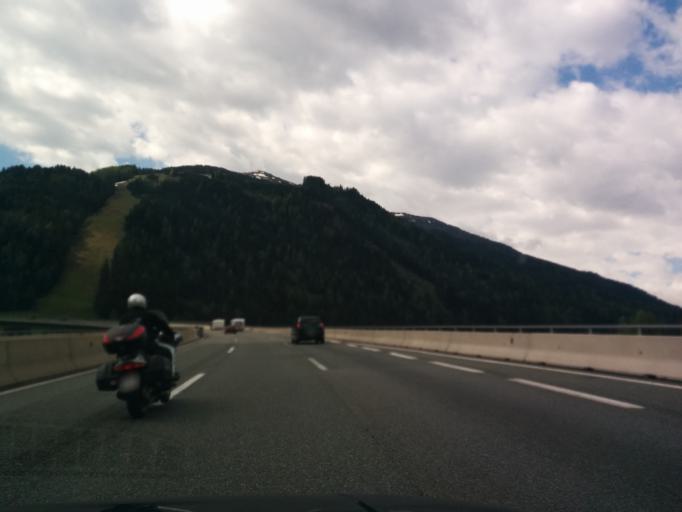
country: AT
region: Tyrol
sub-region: Politischer Bezirk Innsbruck Land
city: Steinach am Brenner
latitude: 47.0906
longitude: 11.4590
